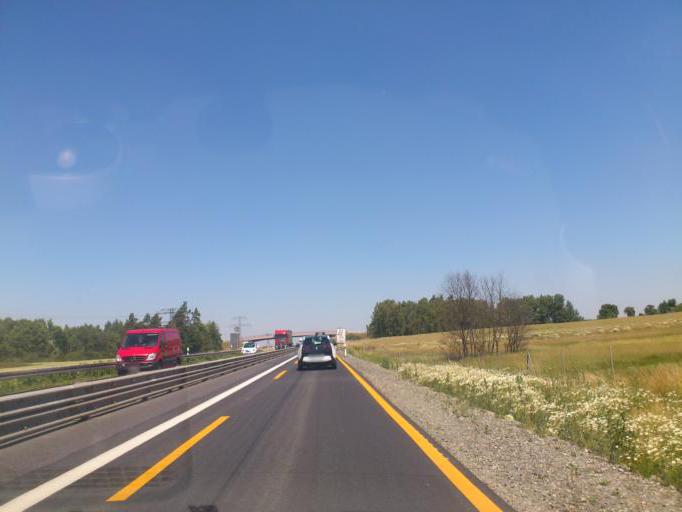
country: DE
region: Saxony
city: Radeburg
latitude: 51.1902
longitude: 13.7428
